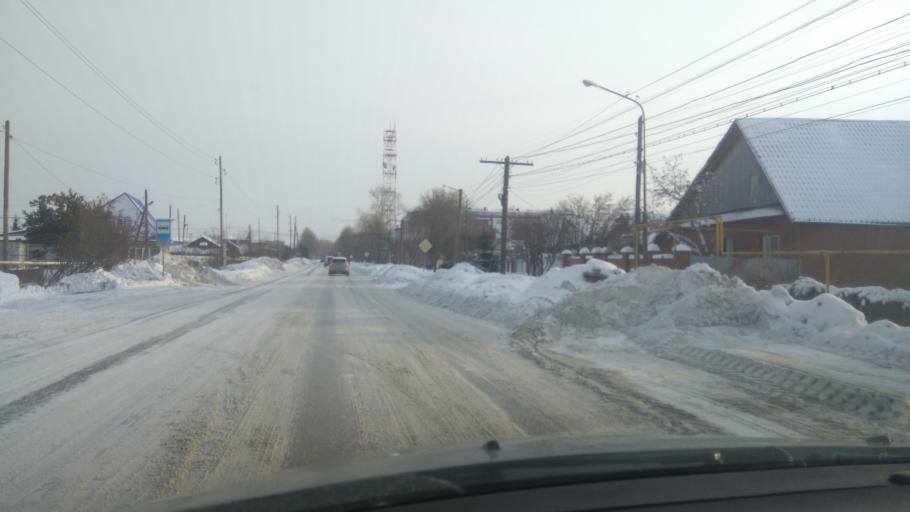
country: RU
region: Sverdlovsk
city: Sukhoy Log
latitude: 56.9094
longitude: 62.0215
